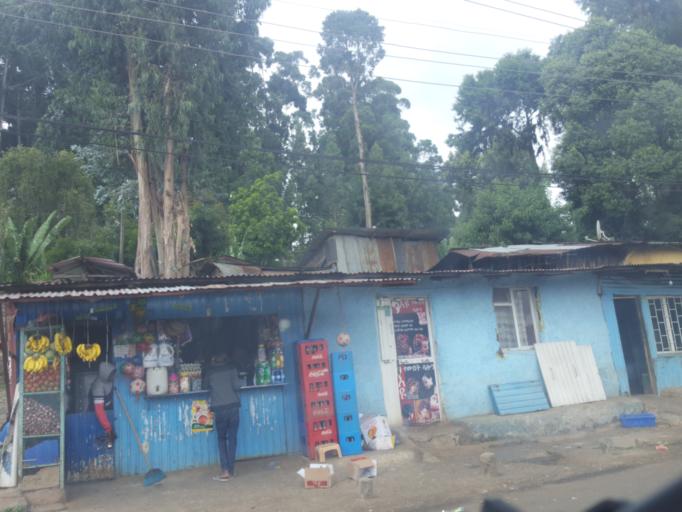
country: ET
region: Adis Abeba
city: Addis Ababa
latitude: 9.0558
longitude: 38.7660
